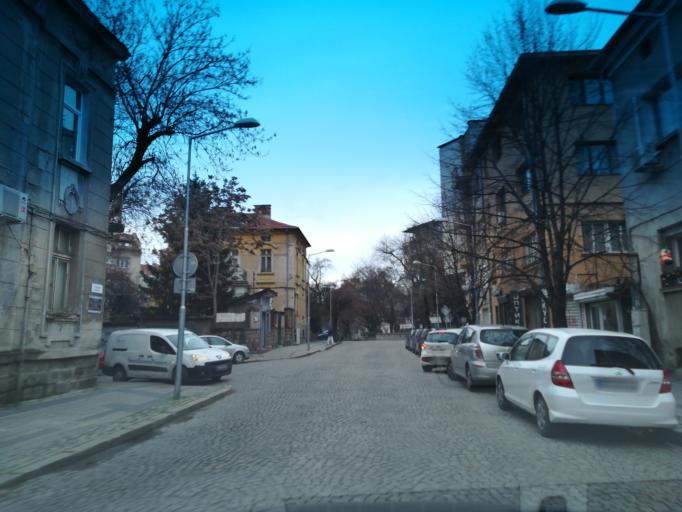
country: BG
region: Plovdiv
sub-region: Obshtina Plovdiv
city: Plovdiv
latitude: 42.1469
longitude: 24.7423
